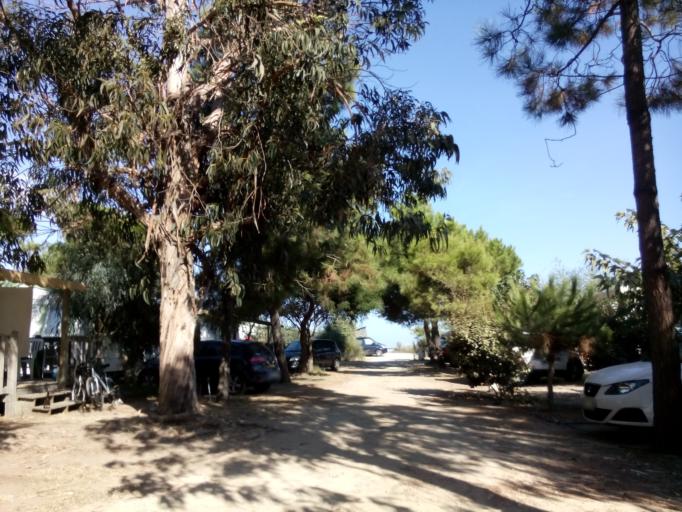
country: FR
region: Corsica
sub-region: Departement de la Haute-Corse
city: Aleria
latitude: 42.1084
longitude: 9.5493
